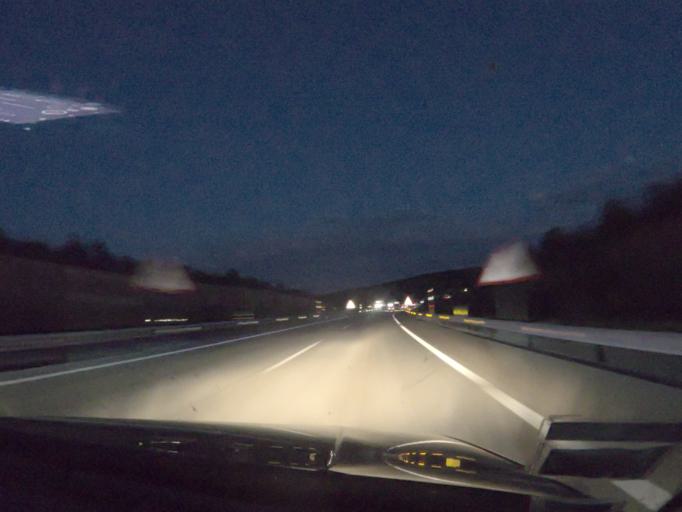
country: ES
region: Castille and Leon
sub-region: Provincia de Leon
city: Brazuelo
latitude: 42.5475
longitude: -6.1658
